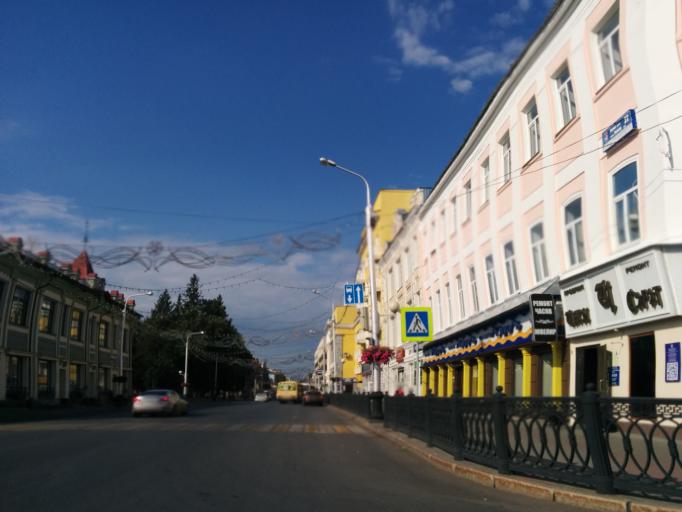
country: RU
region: Bashkortostan
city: Ufa
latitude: 54.7244
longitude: 55.9467
